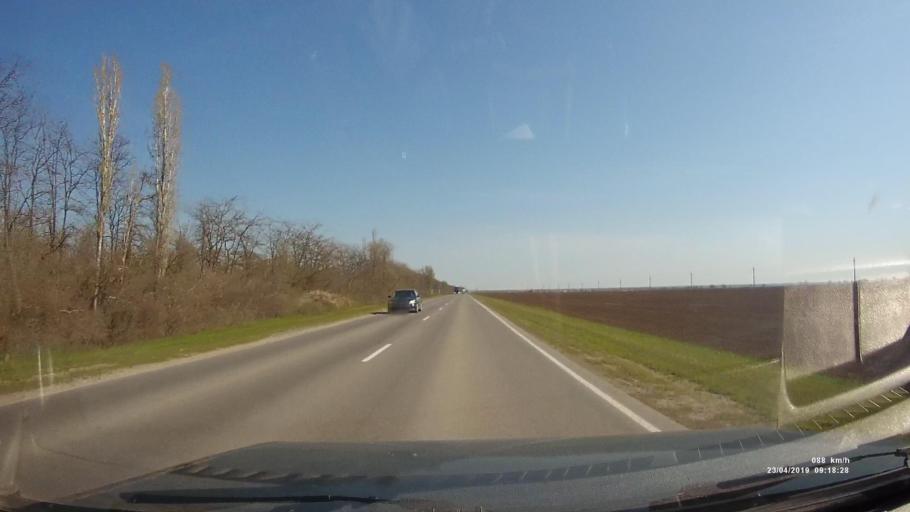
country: RU
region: Rostov
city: Proletarsk
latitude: 46.6641
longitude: 41.6877
